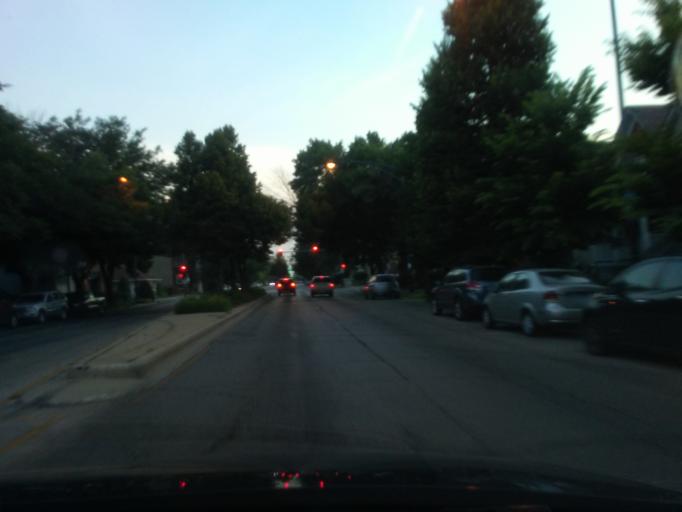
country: US
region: Illinois
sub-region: Cook County
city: Evanston
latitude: 41.9791
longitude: -87.6697
